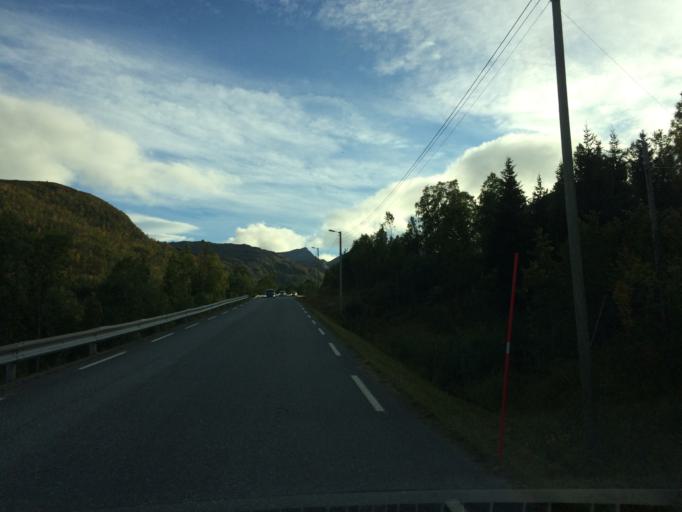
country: NO
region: Troms
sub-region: Tromso
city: Tromso
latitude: 69.6838
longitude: 18.6506
